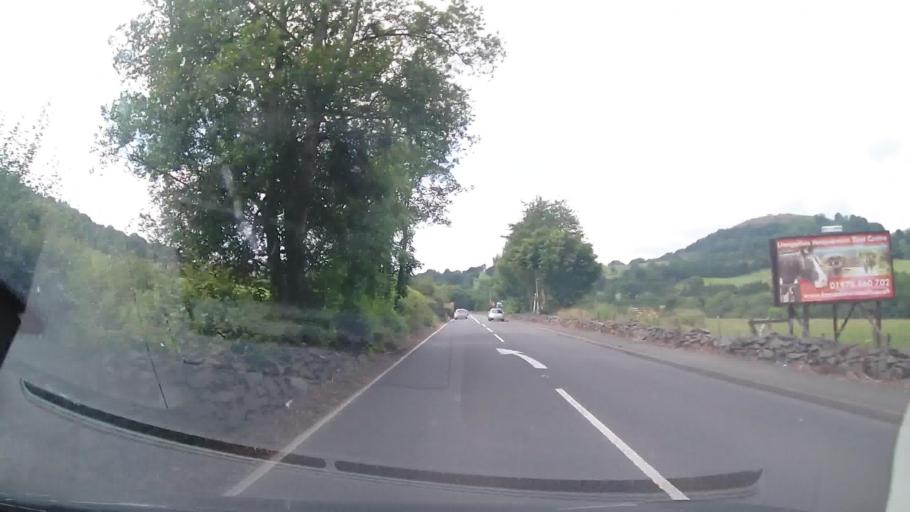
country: GB
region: Wales
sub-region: Denbighshire
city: Llangollen
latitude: 52.9685
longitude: -3.1483
